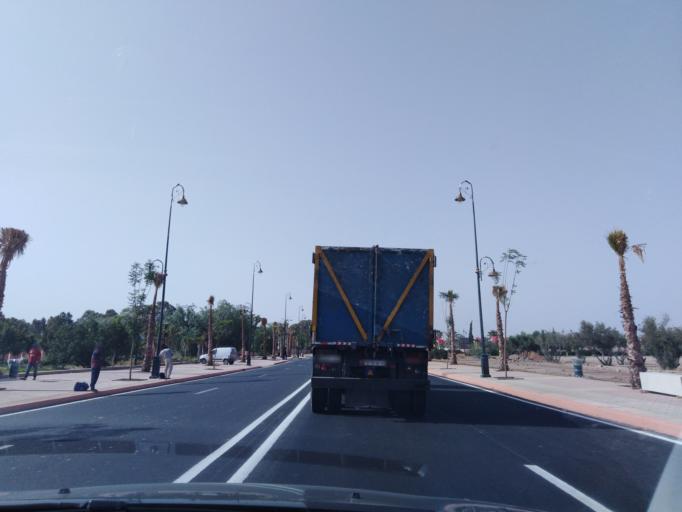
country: MA
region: Marrakech-Tensift-Al Haouz
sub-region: Kelaa-Des-Sraghna
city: Sidi Bou Othmane
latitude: 32.2277
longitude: -7.9570
